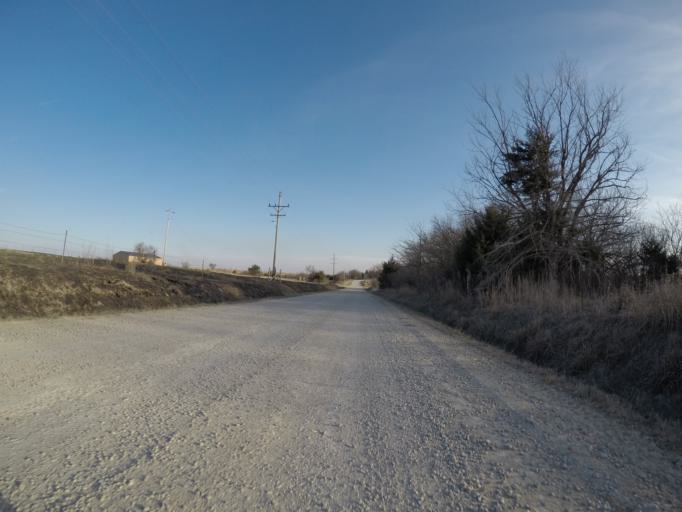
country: US
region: Kansas
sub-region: Riley County
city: Manhattan
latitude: 39.2504
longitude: -96.6818
